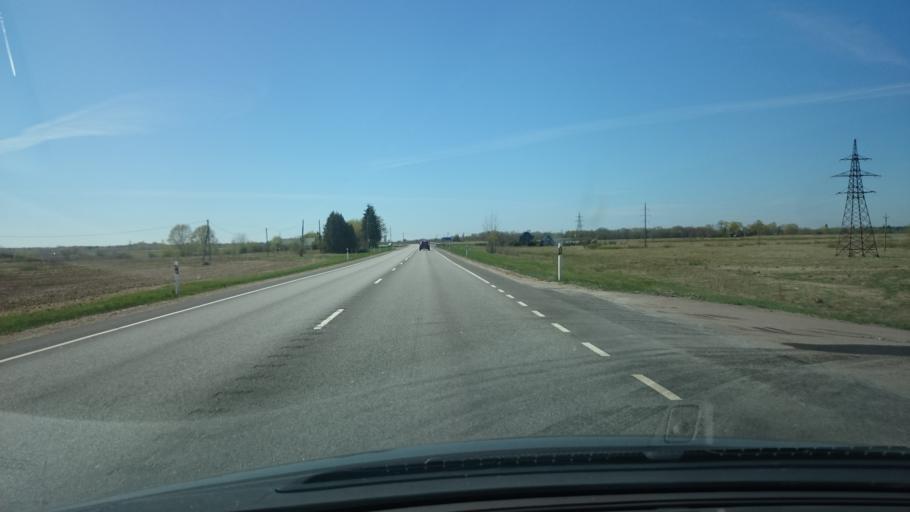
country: EE
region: Ida-Virumaa
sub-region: Narva-Joesuu linn
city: Narva-Joesuu
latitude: 59.4062
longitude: 28.0380
